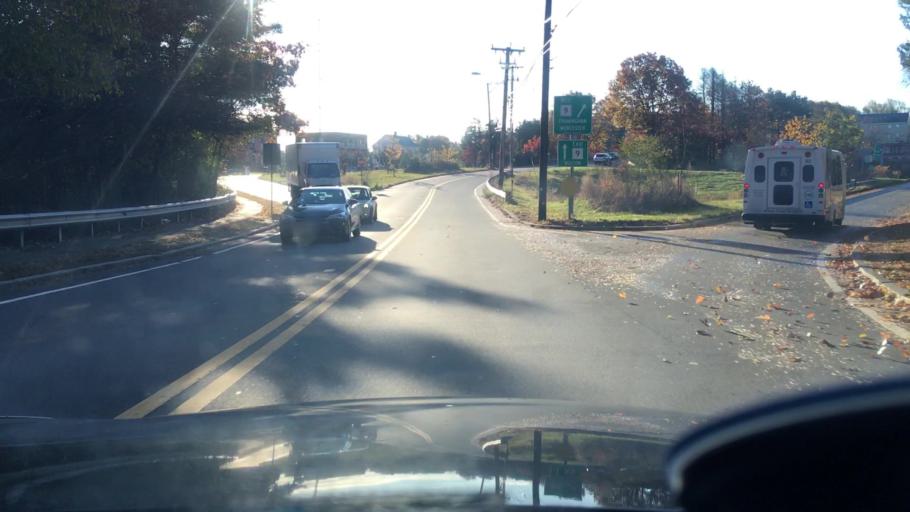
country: US
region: Massachusetts
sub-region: Norfolk County
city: Needham
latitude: 42.3177
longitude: -71.2477
